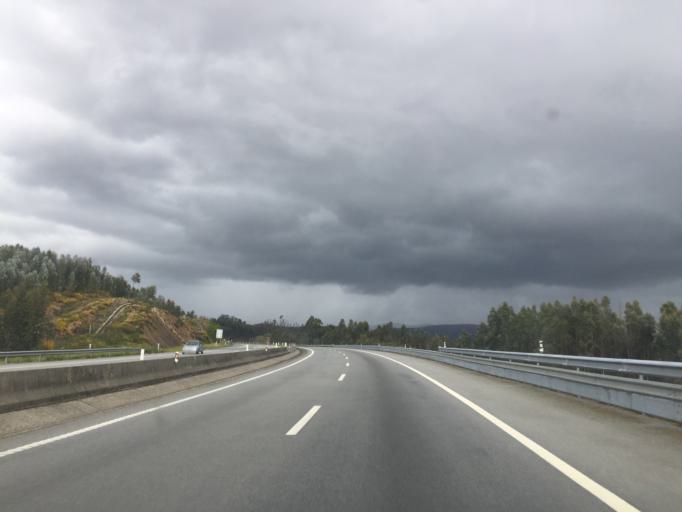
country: PT
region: Aveiro
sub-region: Agueda
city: Valongo
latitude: 40.6646
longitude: -8.4172
